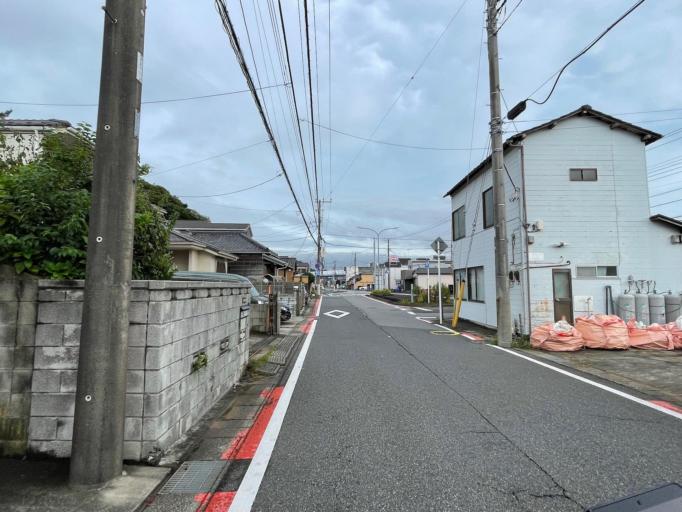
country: JP
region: Chiba
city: Chiba
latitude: 35.6463
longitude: 140.0680
